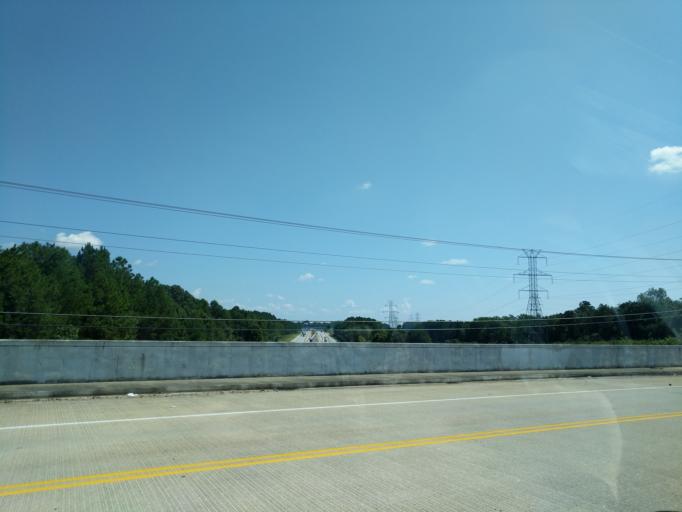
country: US
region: South Carolina
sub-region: Spartanburg County
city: Valley Falls
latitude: 35.0118
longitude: -81.9283
